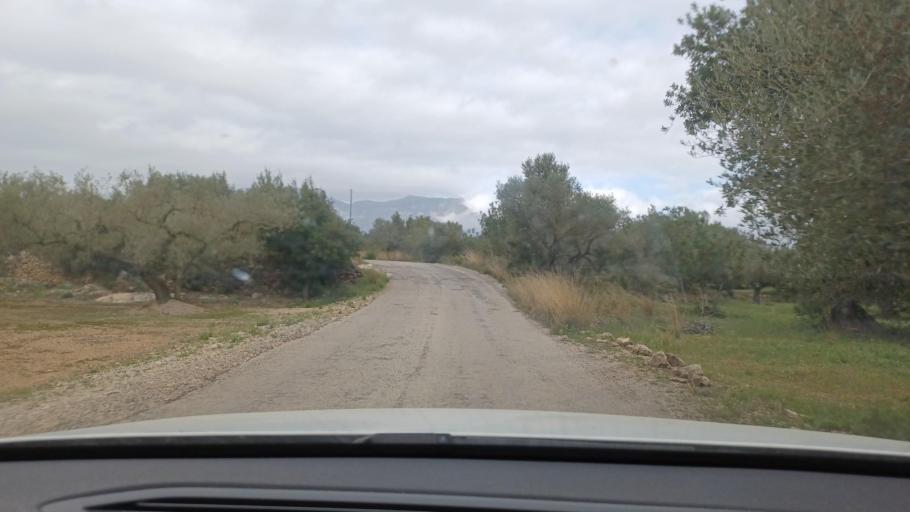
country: ES
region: Catalonia
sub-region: Provincia de Tarragona
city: Tortosa
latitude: 40.7918
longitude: 0.4732
